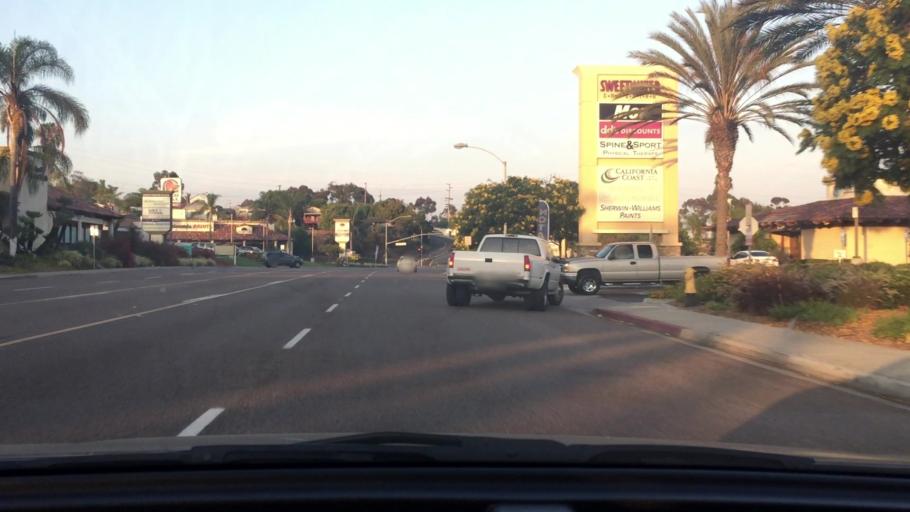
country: US
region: California
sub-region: San Diego County
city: Chula Vista
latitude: 32.6613
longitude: -117.0826
